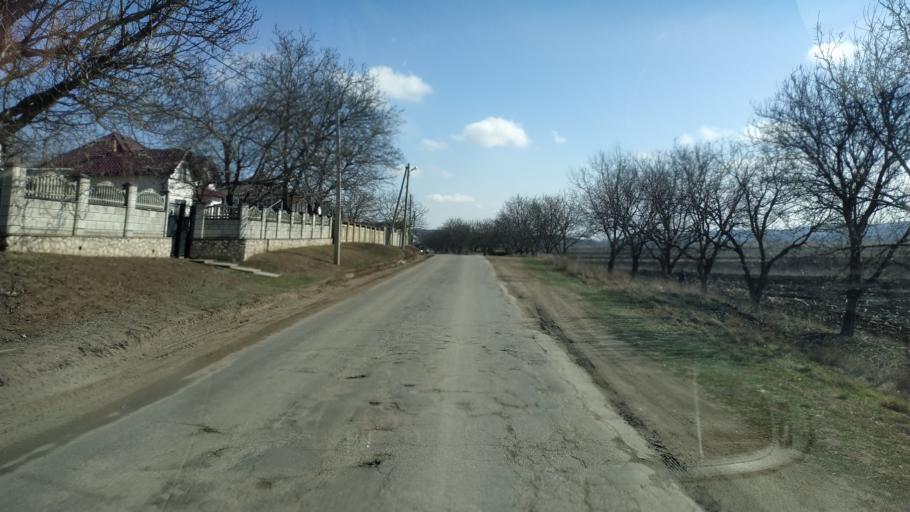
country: MD
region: Laloveni
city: Ialoveni
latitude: 46.9314
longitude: 28.6658
